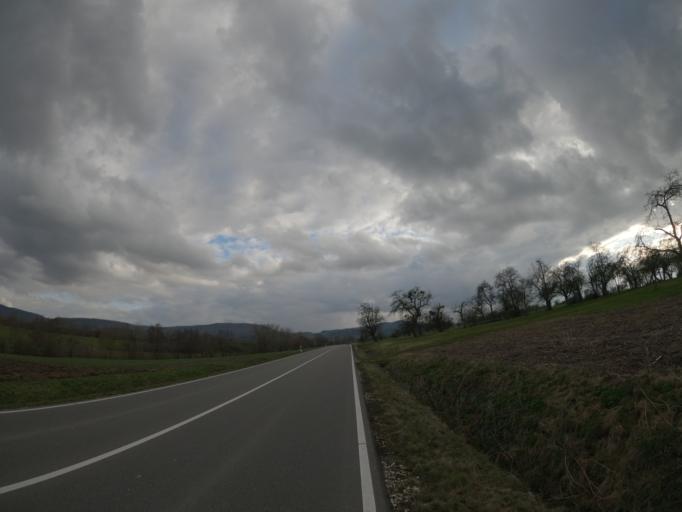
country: DE
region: Baden-Wuerttemberg
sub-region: Regierungsbezirk Stuttgart
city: Boll
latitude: 48.6595
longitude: 9.6143
